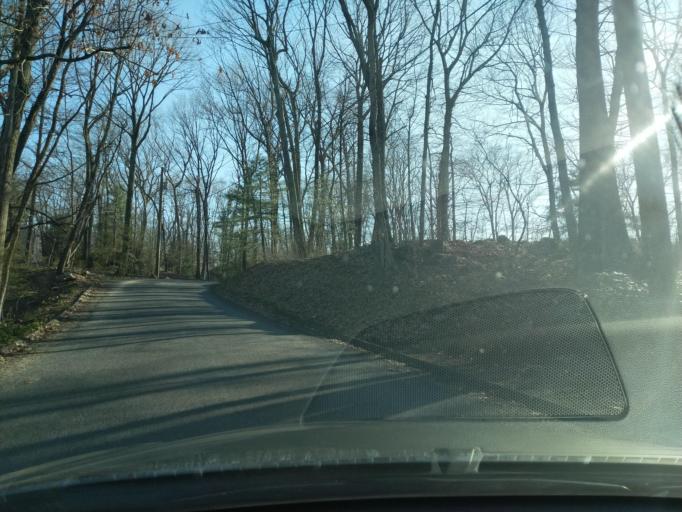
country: US
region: Connecticut
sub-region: Fairfield County
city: Newtown
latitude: 41.3847
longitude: -73.2892
